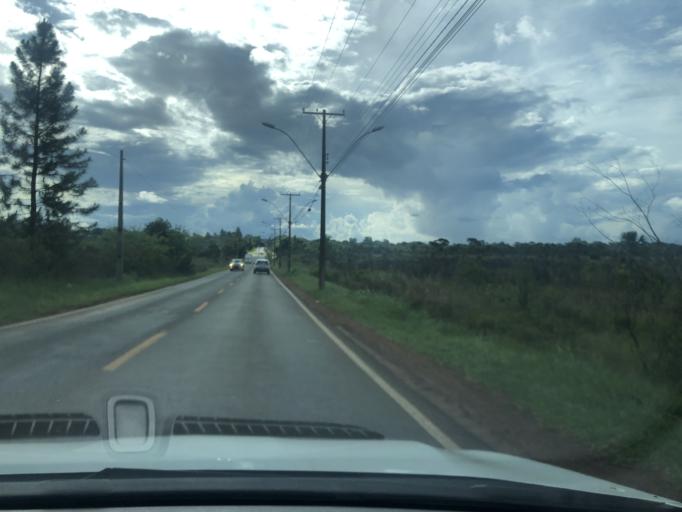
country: BR
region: Federal District
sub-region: Brasilia
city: Brasilia
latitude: -15.8957
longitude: -47.9403
